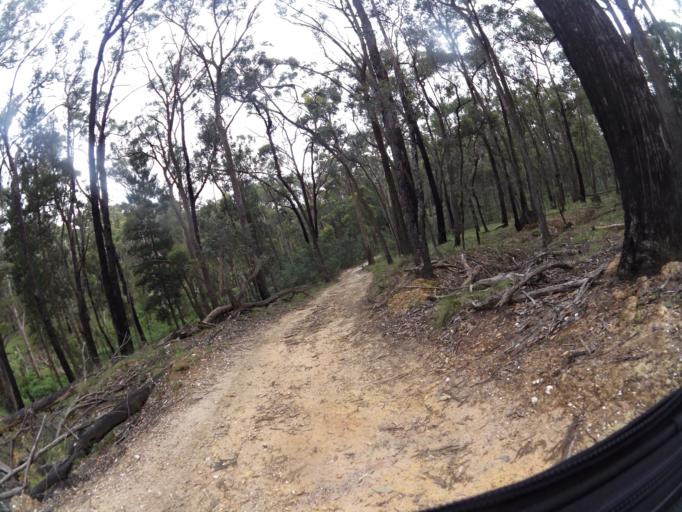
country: AU
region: Victoria
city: Brown Hill
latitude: -37.4895
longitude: 143.9070
